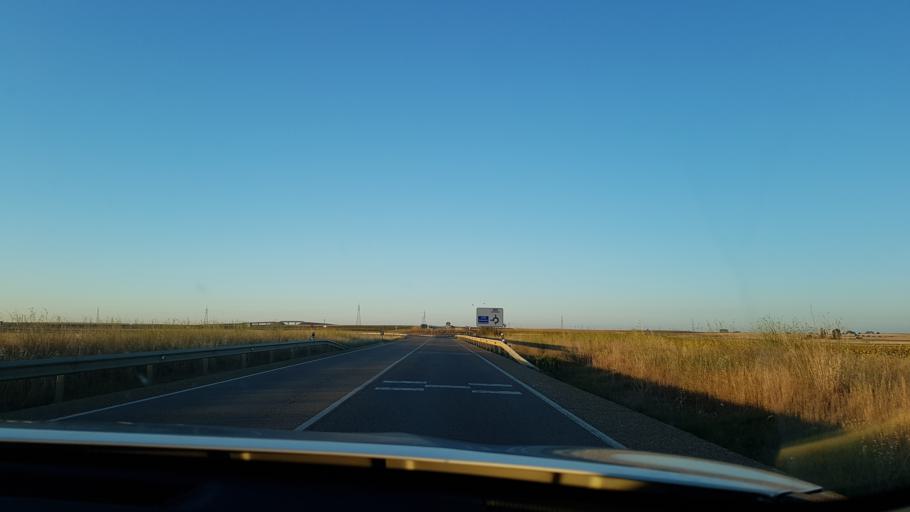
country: ES
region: Castille and Leon
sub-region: Provincia de Zamora
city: Montamarta
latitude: 41.6337
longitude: -5.7980
